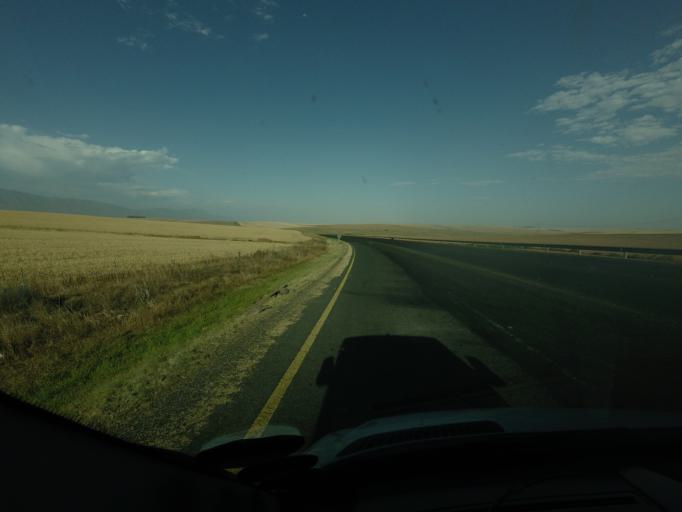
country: ZA
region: Western Cape
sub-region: Overberg District Municipality
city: Swellendam
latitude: -34.1077
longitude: 20.3511
